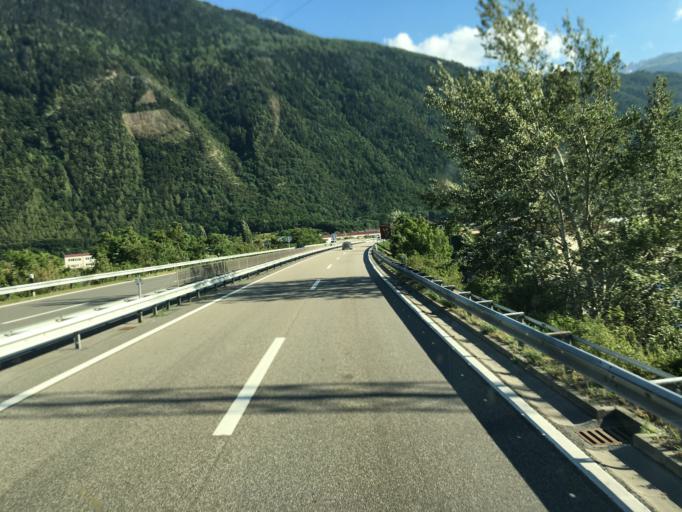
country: CH
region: Valais
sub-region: Martigny District
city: Martigny-Ville
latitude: 46.1107
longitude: 7.0974
